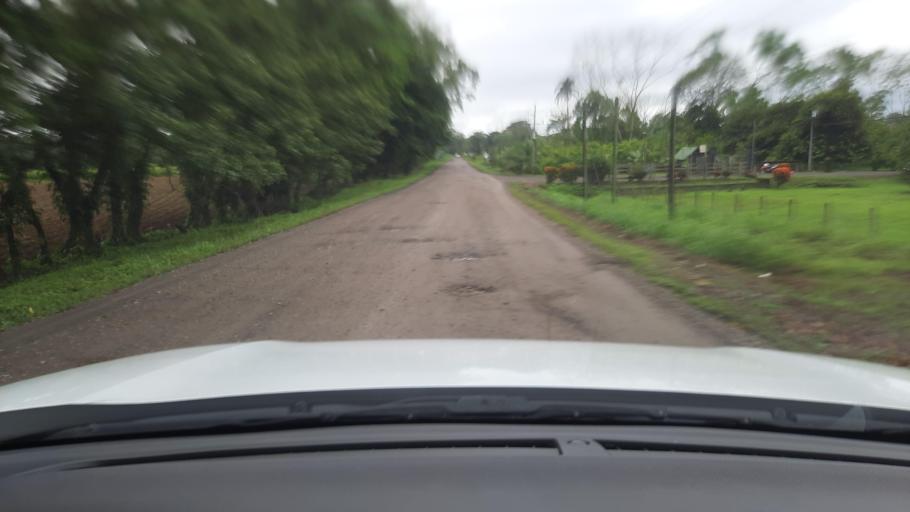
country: CR
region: Alajuela
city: San Jose
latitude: 10.9845
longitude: -85.2714
